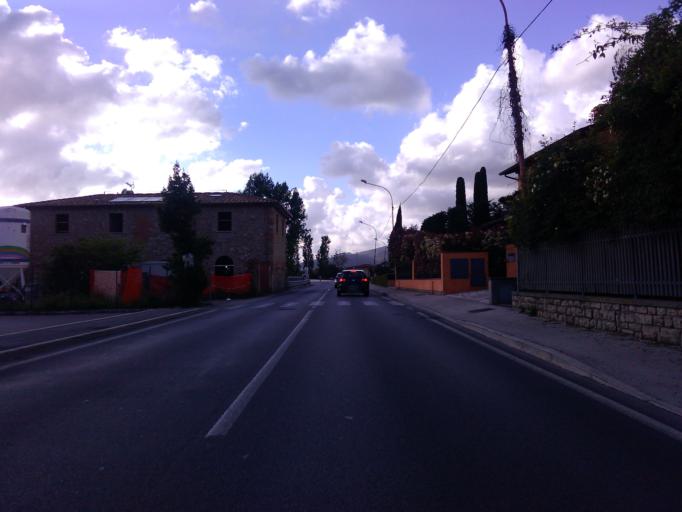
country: IT
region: Tuscany
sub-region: Provincia di Lucca
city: Pietrasanta
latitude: 43.9649
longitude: 10.2227
